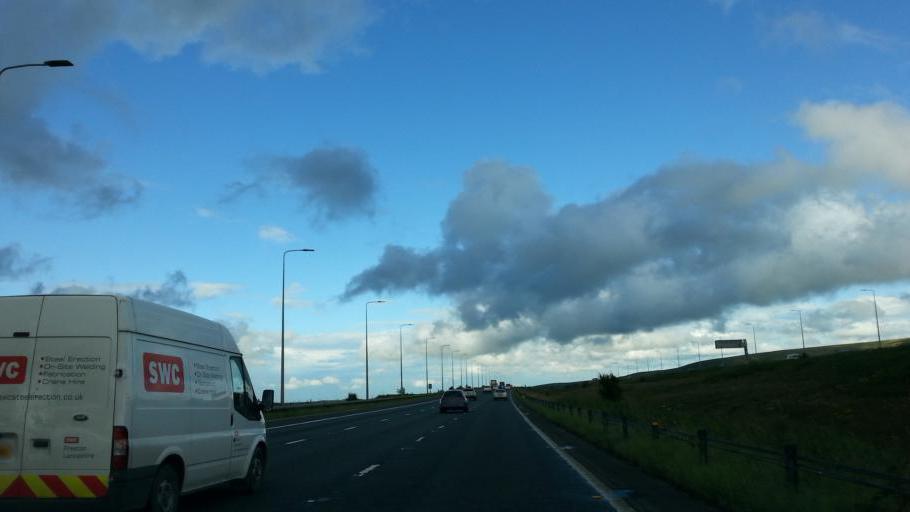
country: GB
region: England
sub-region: Borough of Oldham
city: Diggle
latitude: 53.6324
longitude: -2.0014
